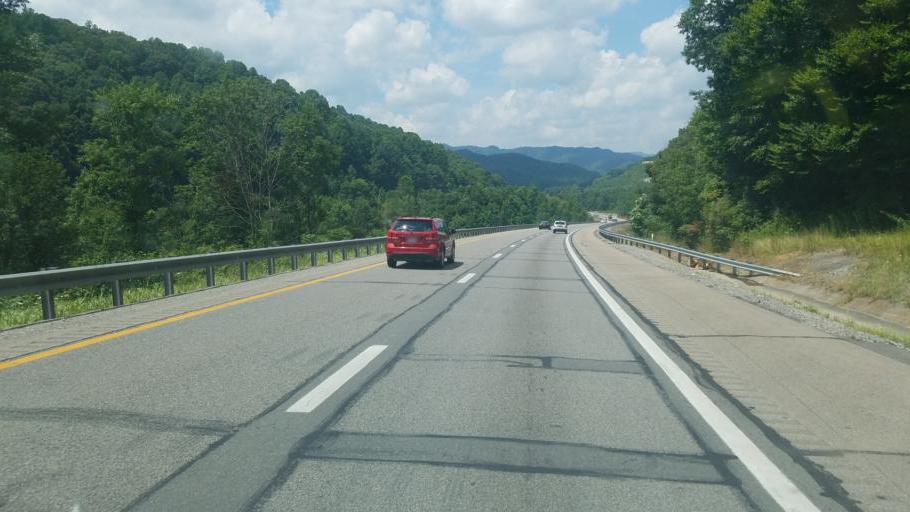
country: US
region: West Virginia
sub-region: Raleigh County
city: Prosperity
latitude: 37.8518
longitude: -81.2505
